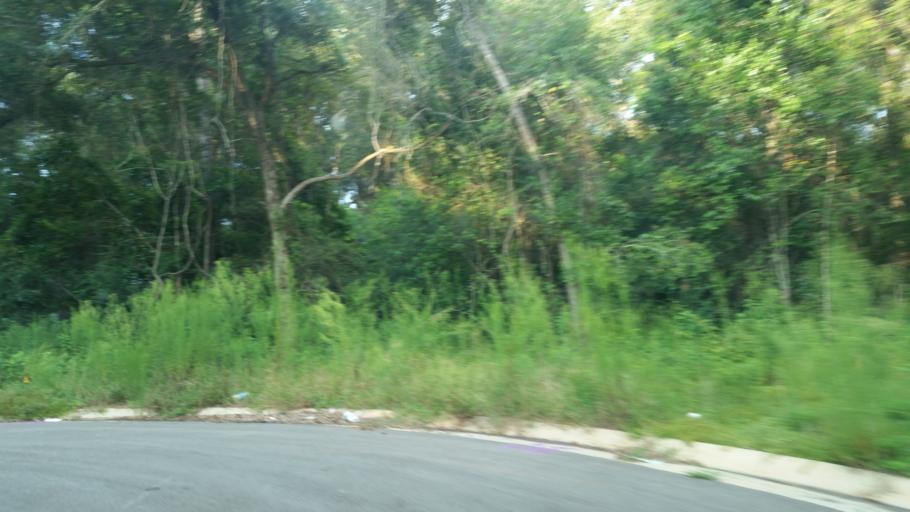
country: US
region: Florida
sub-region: Santa Rosa County
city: Pace
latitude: 30.6166
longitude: -87.1353
